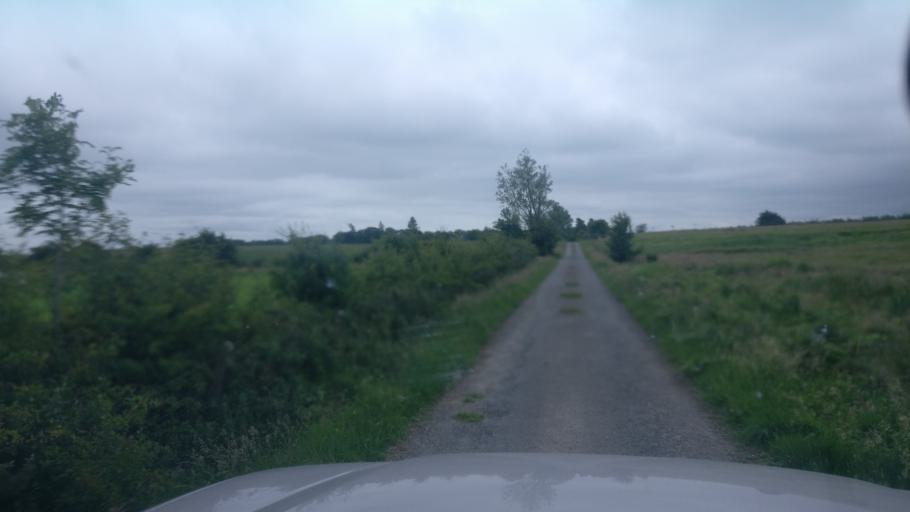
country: IE
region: Connaught
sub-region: County Galway
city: Ballinasloe
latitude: 53.2981
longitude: -8.3625
